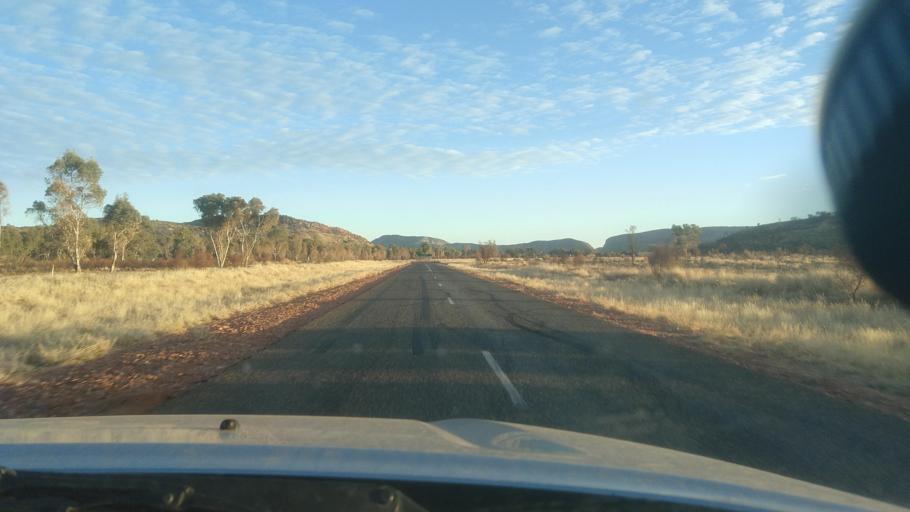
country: AU
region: Northern Territory
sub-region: Alice Springs
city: Alice Springs
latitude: -23.7341
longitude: 133.7390
